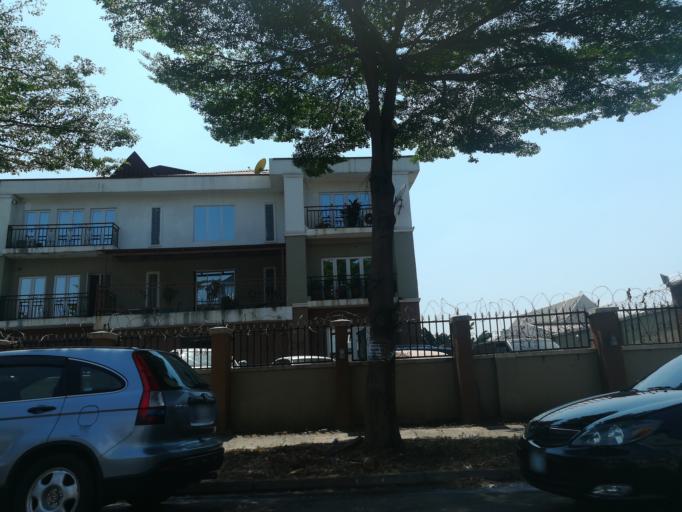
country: NG
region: Abuja Federal Capital Territory
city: Abuja
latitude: 9.0701
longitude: 7.4502
